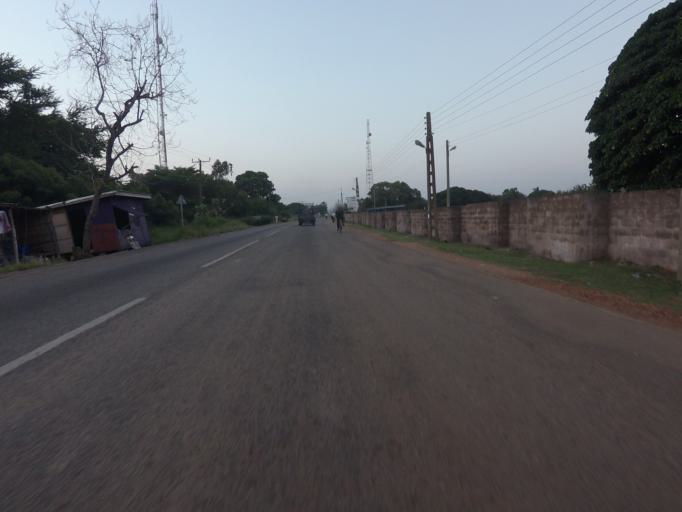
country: GH
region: Volta
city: Keta
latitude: 5.8961
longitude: 0.9872
